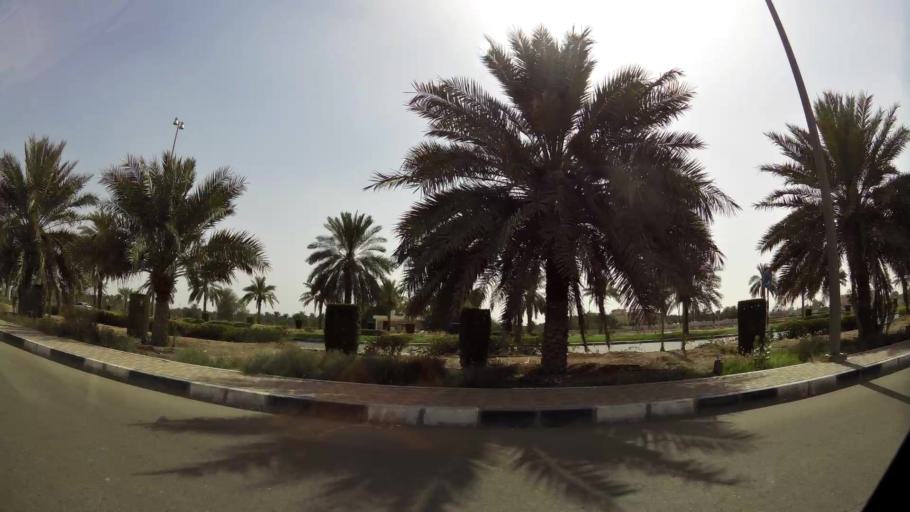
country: AE
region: Abu Dhabi
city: Al Ain
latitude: 24.2316
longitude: 55.6803
